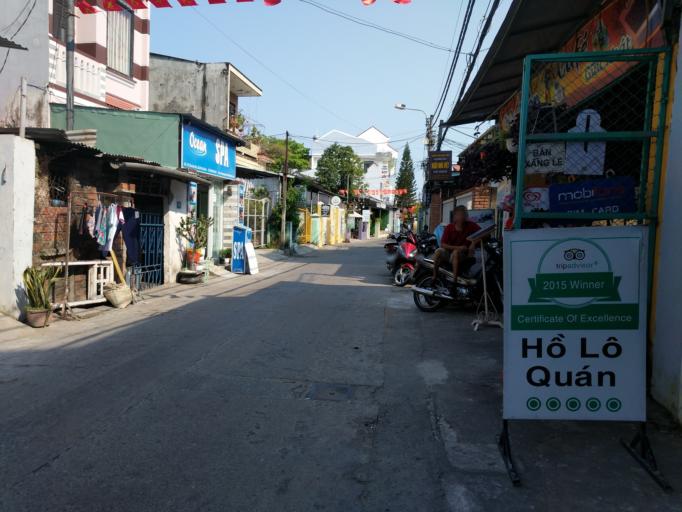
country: VN
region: Quang Nam
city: Hoi An
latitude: 15.8835
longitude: 108.3261
